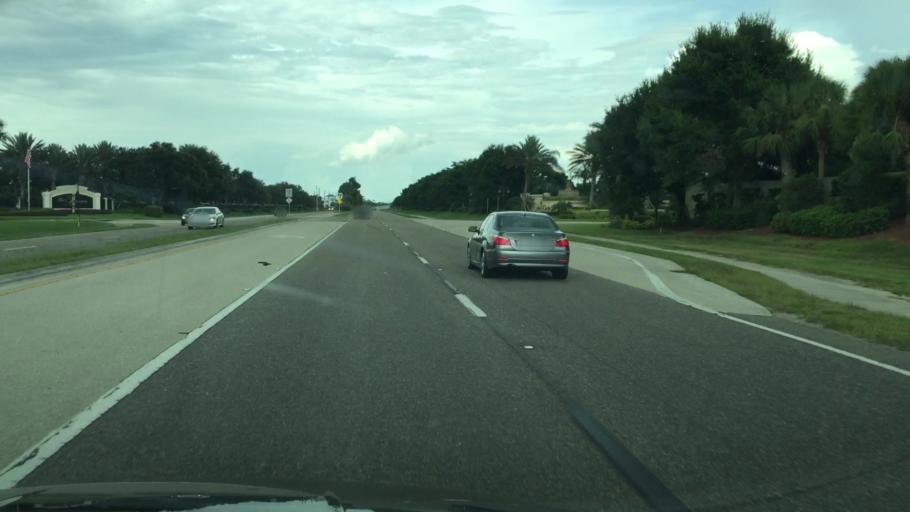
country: US
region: Florida
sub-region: Lee County
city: Estero
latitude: 26.4491
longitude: -81.8020
